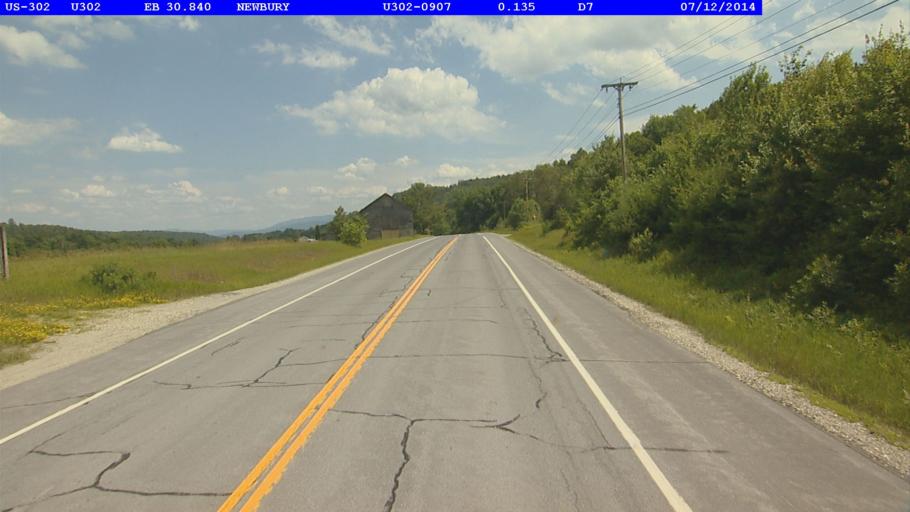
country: US
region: New Hampshire
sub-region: Grafton County
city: Woodsville
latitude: 44.1754
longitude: -72.1149
